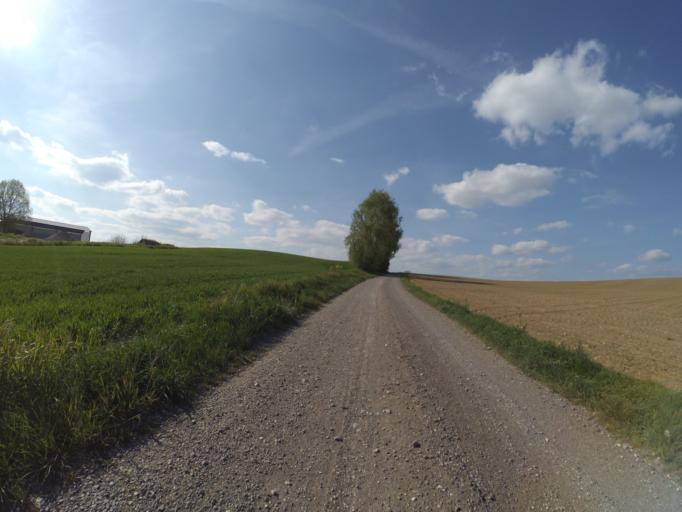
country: CH
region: Thurgau
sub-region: Frauenfeld District
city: Diessenhofen
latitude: 47.6612
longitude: 8.7541
